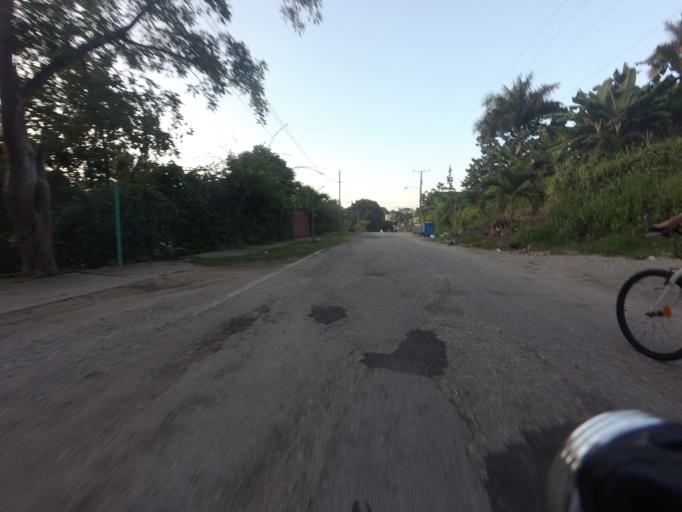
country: CU
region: La Habana
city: Cerro
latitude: 23.1141
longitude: -82.4058
